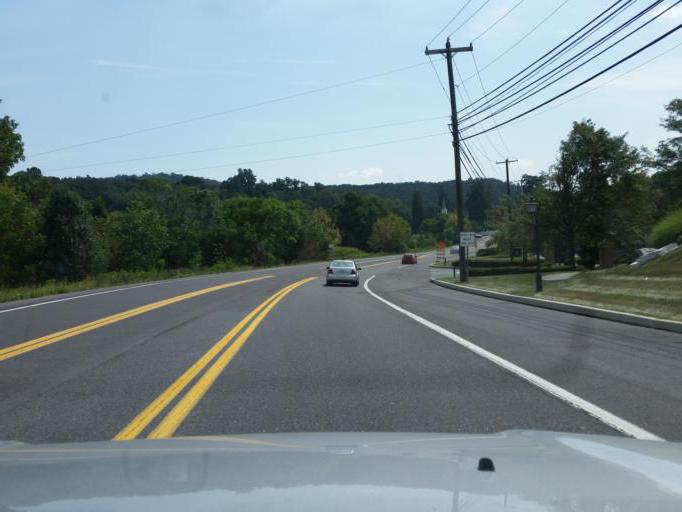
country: US
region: Pennsylvania
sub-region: Dauphin County
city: Hummelstown
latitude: 40.2480
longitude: -76.7074
